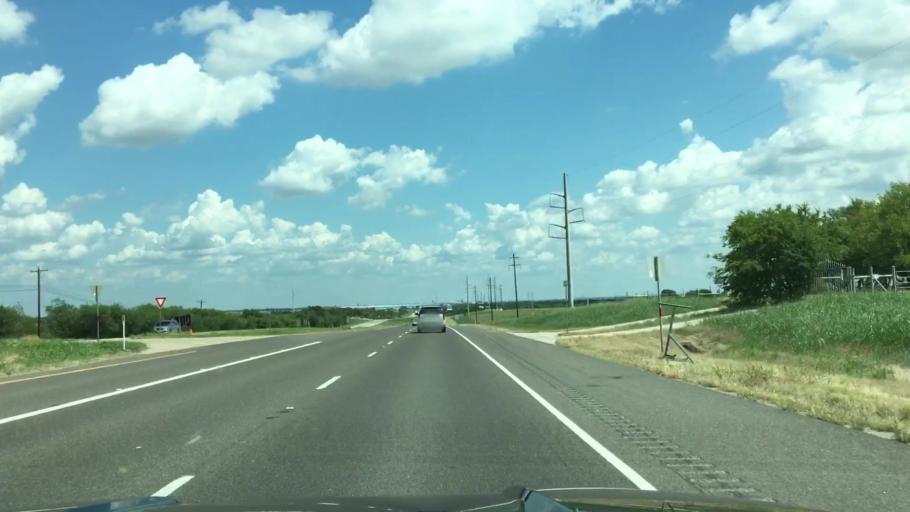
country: US
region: Texas
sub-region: Wise County
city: Rhome
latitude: 33.0366
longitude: -97.4175
